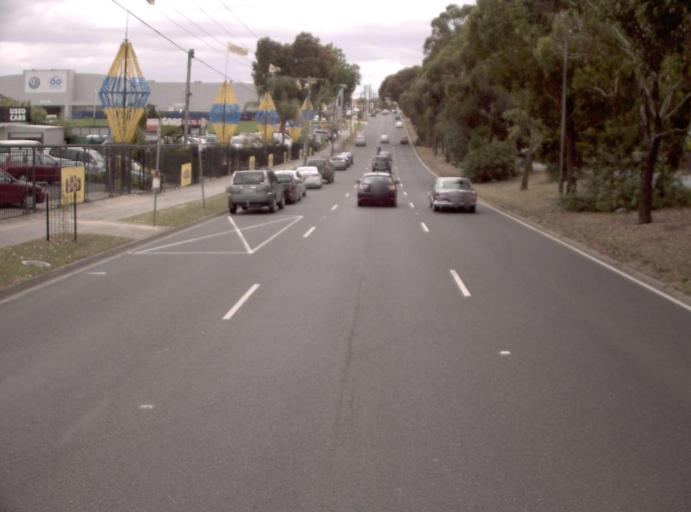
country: AU
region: Victoria
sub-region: Maroondah
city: Ringwood East
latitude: -37.8014
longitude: 145.2491
